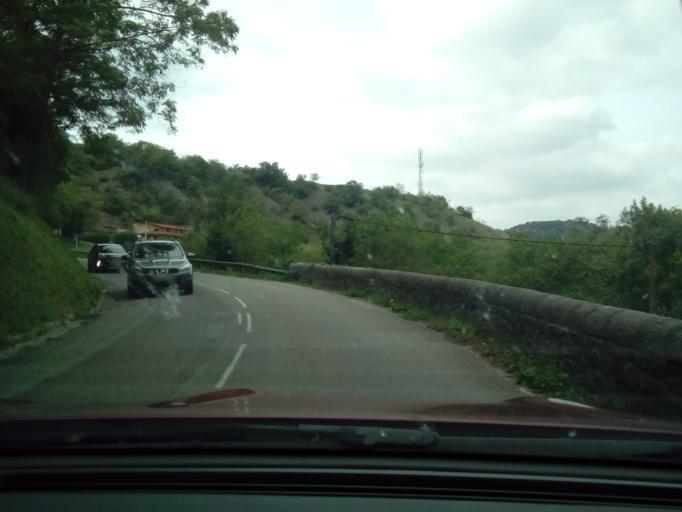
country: FR
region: Rhone-Alpes
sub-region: Departement de l'Isere
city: Pont-en-Royans
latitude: 45.0561
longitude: 5.3425
